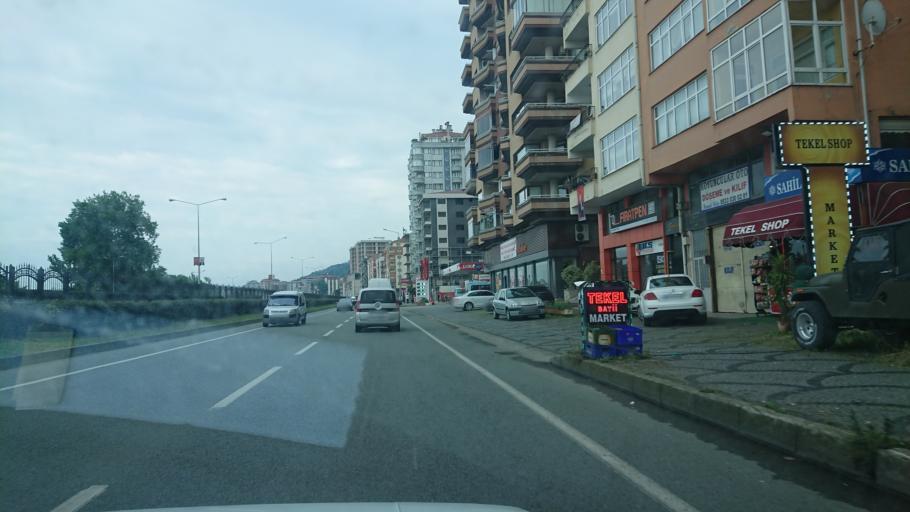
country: TR
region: Rize
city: Rize
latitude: 41.0265
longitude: 40.5412
